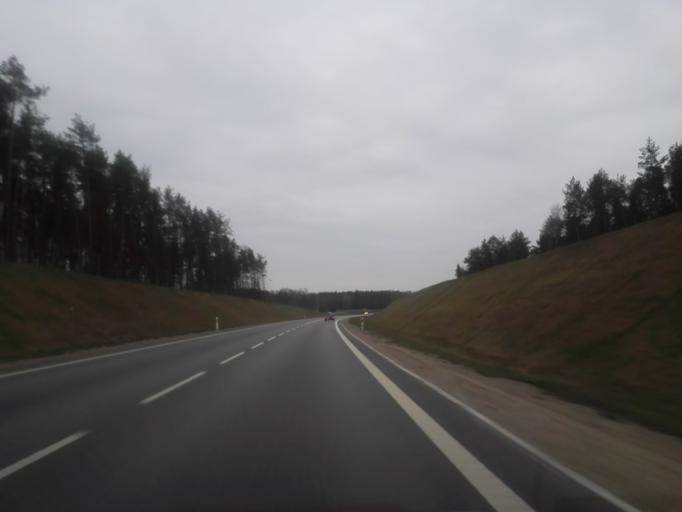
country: PL
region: Podlasie
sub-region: Powiat kolnenski
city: Stawiski
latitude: 53.3604
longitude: 22.1602
